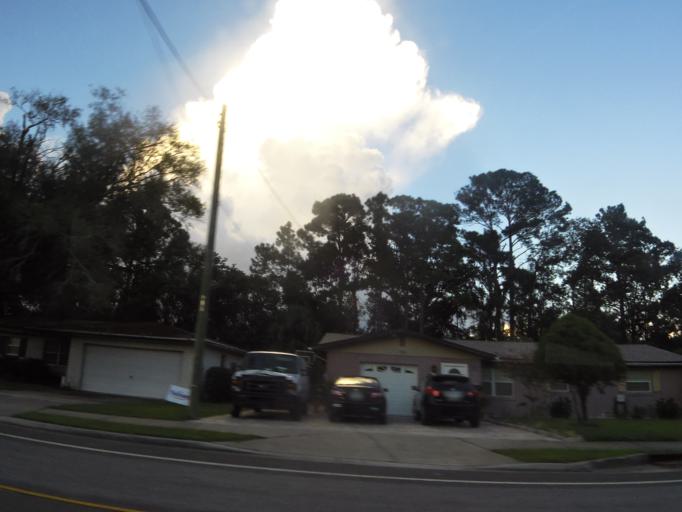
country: US
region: Florida
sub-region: Duval County
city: Jacksonville
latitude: 30.2375
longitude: -81.6068
